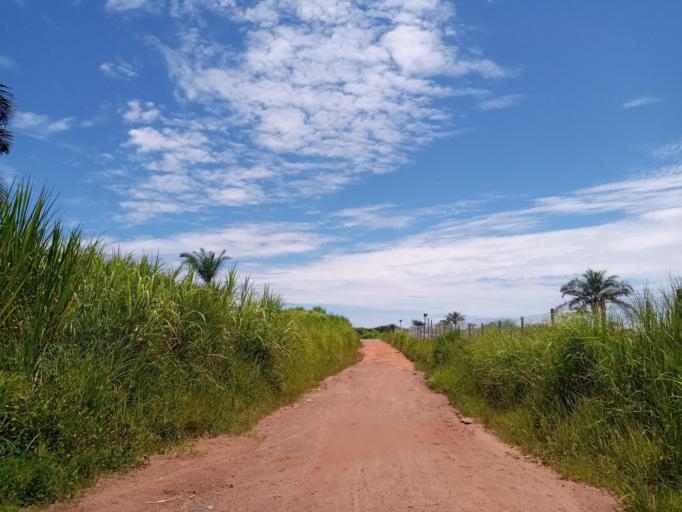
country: SL
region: Eastern Province
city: Koidu
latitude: 8.6538
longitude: -10.9500
